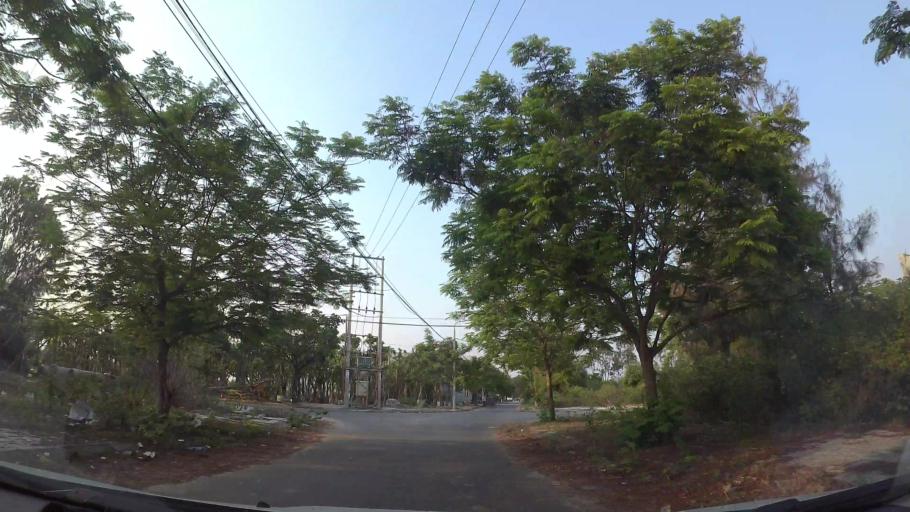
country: VN
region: Da Nang
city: Ngu Hanh Son
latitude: 15.9840
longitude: 108.2536
